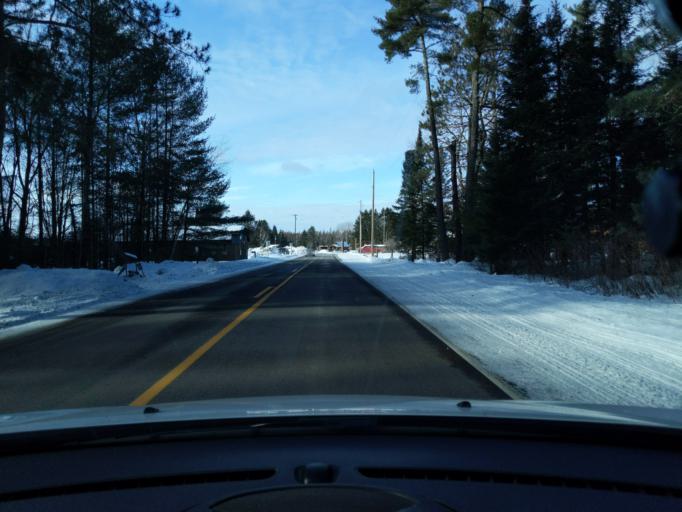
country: US
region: Wisconsin
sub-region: Sawyer County
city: Little Round Lake
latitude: 46.1209
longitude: -91.3592
